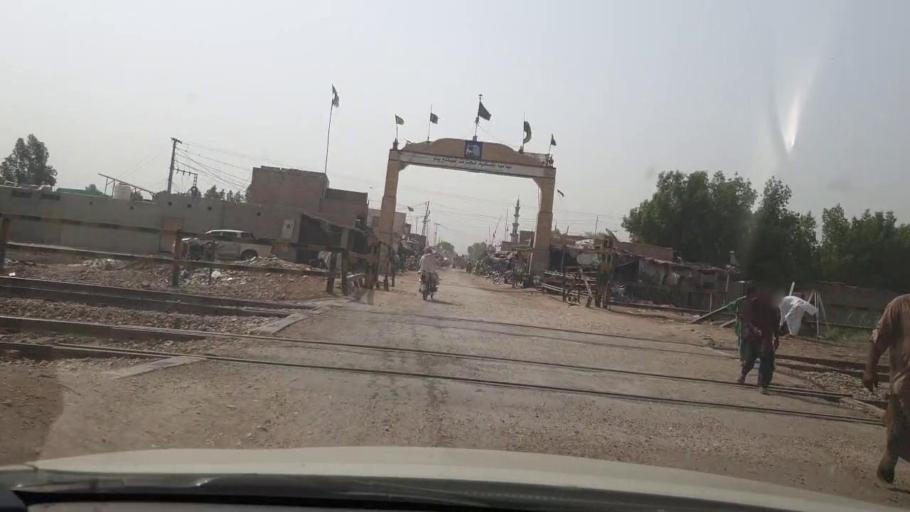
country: PK
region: Sindh
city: Kot Diji
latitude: 27.4322
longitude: 68.6514
